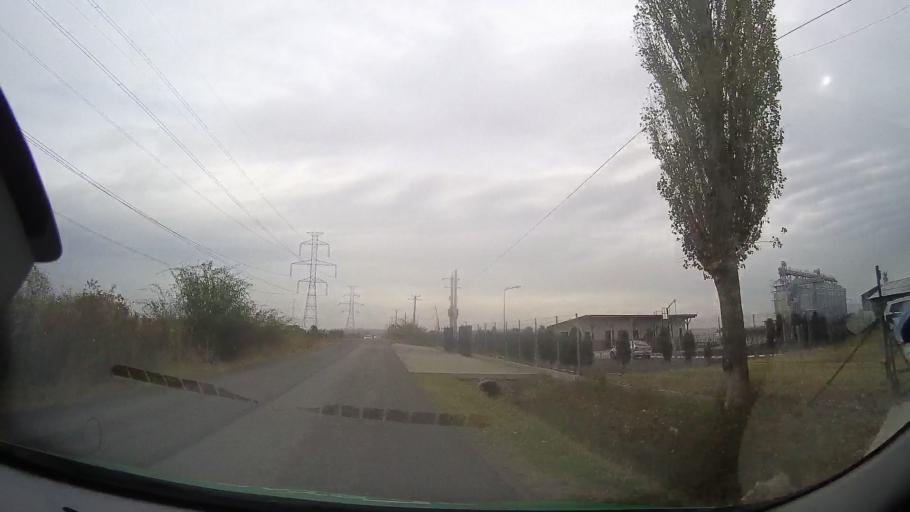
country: RO
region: Prahova
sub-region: Comuna Valea Calugareasca
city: Pantazi
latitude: 44.9289
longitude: 26.1477
